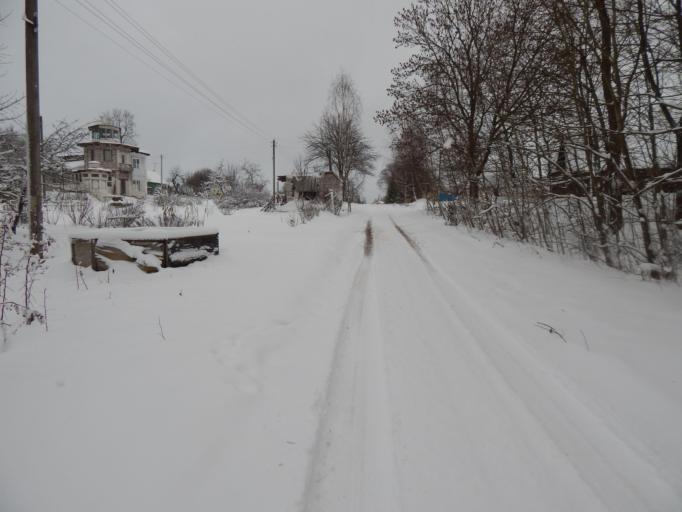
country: BY
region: Minsk
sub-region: Minski Rayon
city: Krasnaye
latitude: 54.1309
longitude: 27.0719
